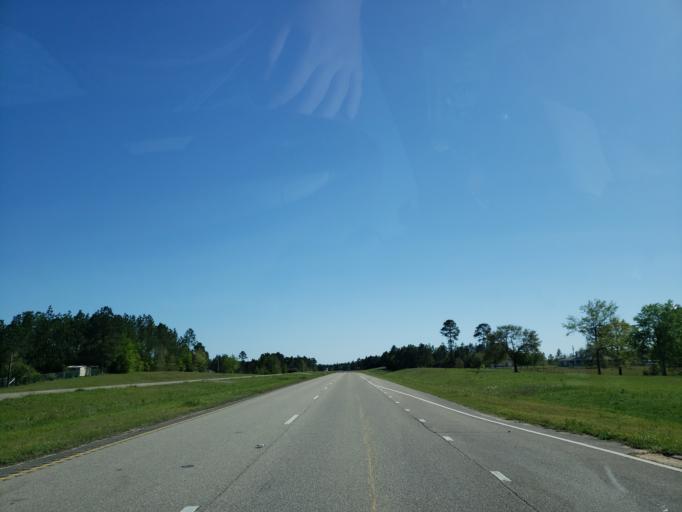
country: US
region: Mississippi
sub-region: Harrison County
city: Lyman
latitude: 30.5294
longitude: -89.0327
